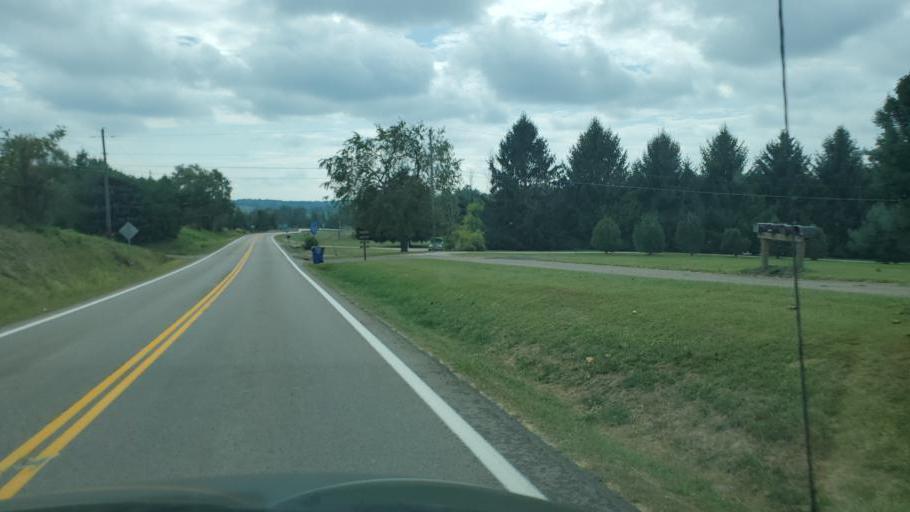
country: US
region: Ohio
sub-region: Perry County
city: Somerset
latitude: 39.9398
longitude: -82.2554
